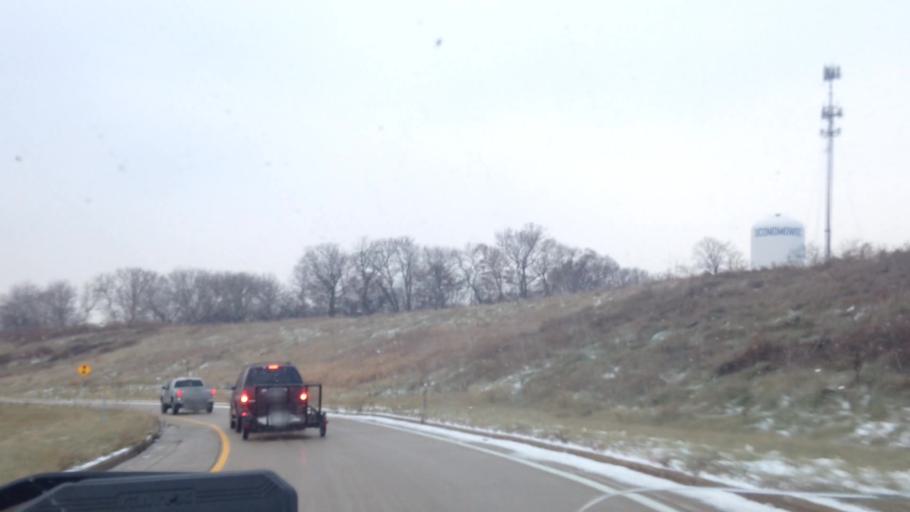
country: US
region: Wisconsin
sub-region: Waukesha County
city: Oconomowoc
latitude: 43.1099
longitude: -88.4810
